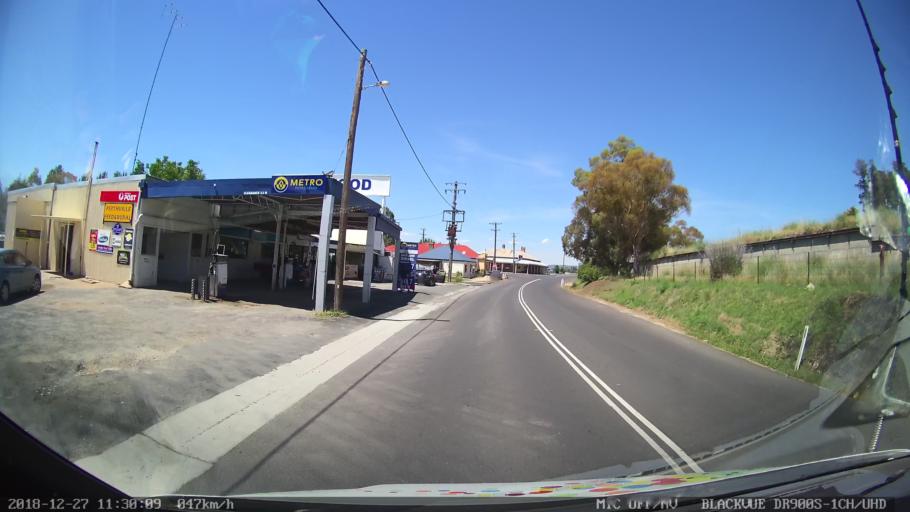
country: AU
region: New South Wales
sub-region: Bathurst Regional
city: Perthville
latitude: -33.4857
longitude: 149.5474
